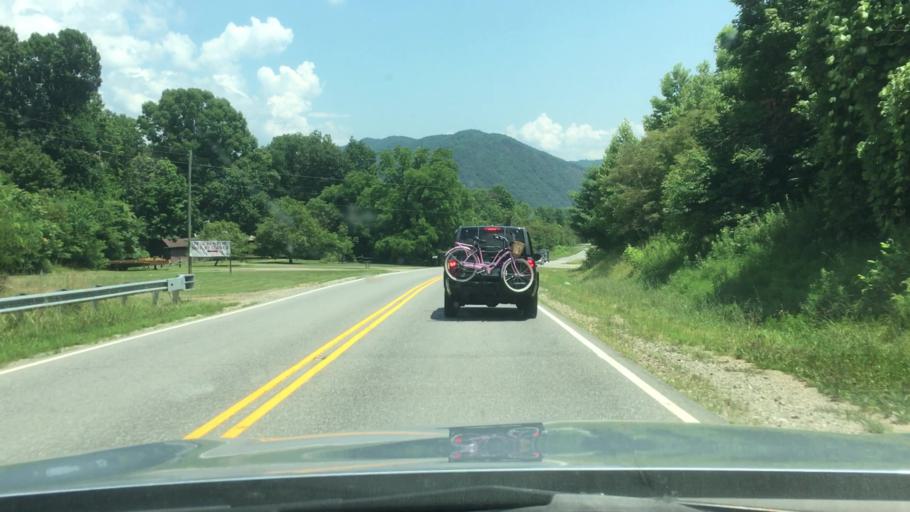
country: US
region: North Carolina
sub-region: Madison County
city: Marshall
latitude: 35.8983
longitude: -82.8439
